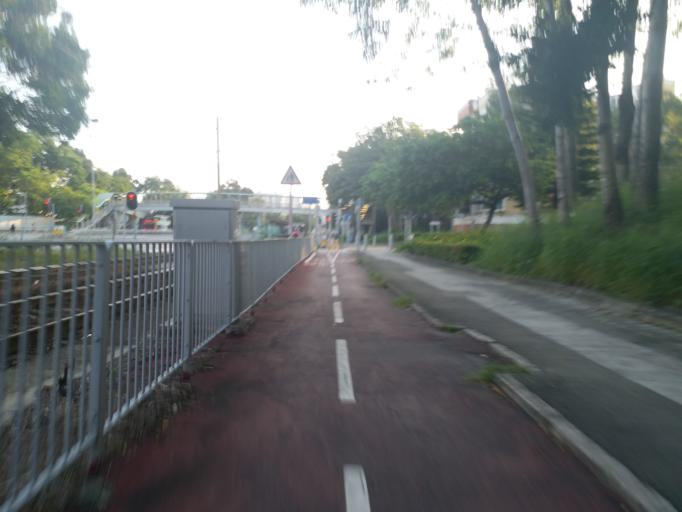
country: HK
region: Yuen Long
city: Yuen Long Kau Hui
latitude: 22.4411
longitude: 114.0085
